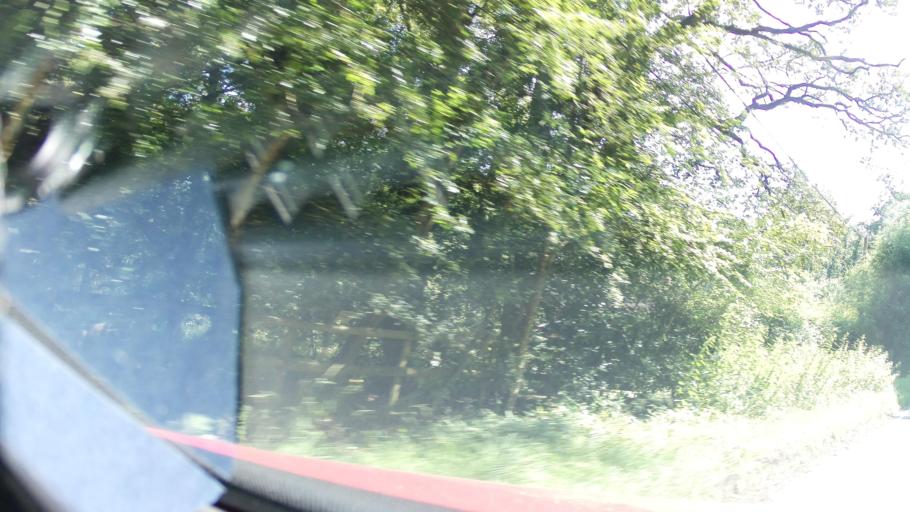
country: GB
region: England
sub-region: West Berkshire
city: Winterbourne
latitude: 51.4426
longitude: -1.3344
